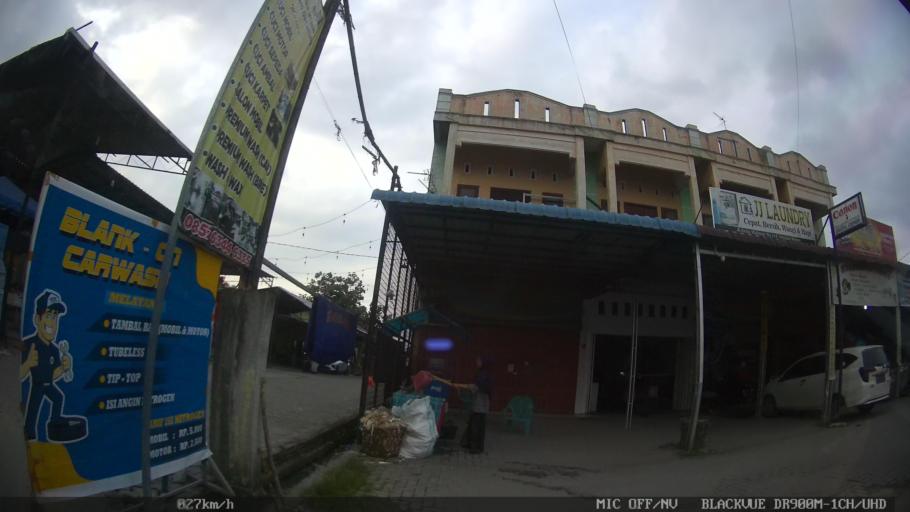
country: ID
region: North Sumatra
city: Sunggal
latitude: 3.5641
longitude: 98.6011
